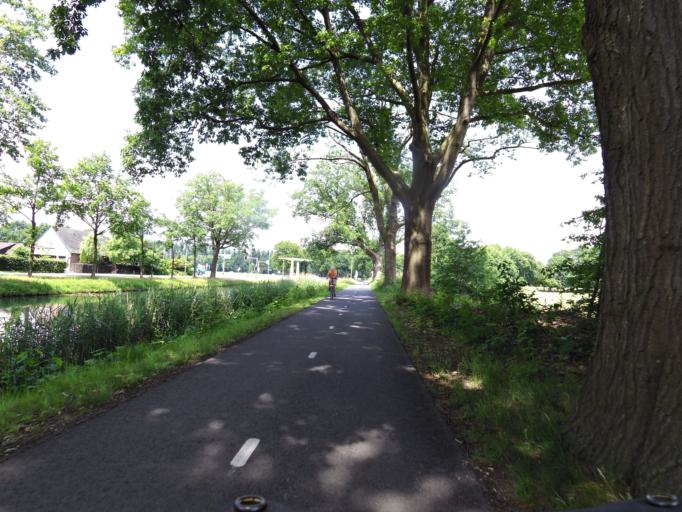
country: NL
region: Gelderland
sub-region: Gemeente Apeldoorn
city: Loenen
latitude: 52.1390
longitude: 6.0414
